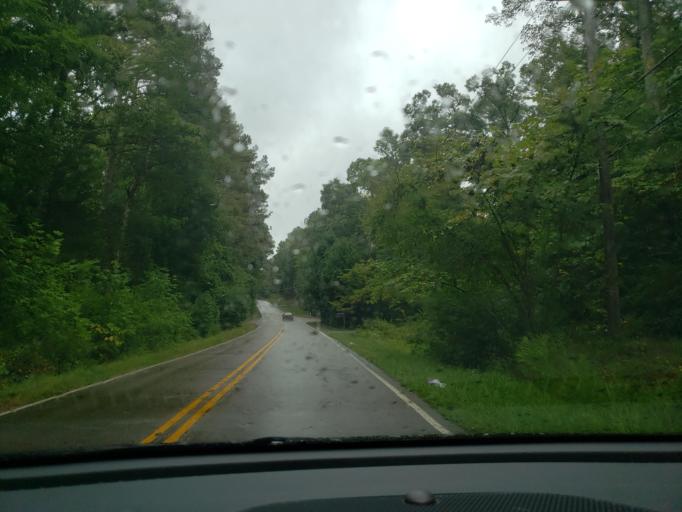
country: US
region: North Carolina
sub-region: Durham County
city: Durham
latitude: 35.9800
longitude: -78.9499
